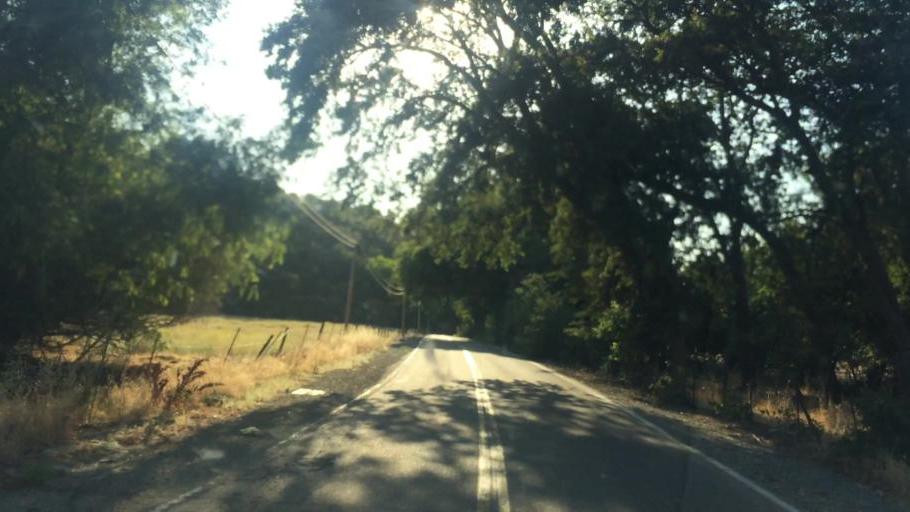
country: US
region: California
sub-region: Amador County
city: Plymouth
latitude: 38.4833
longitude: -120.8784
